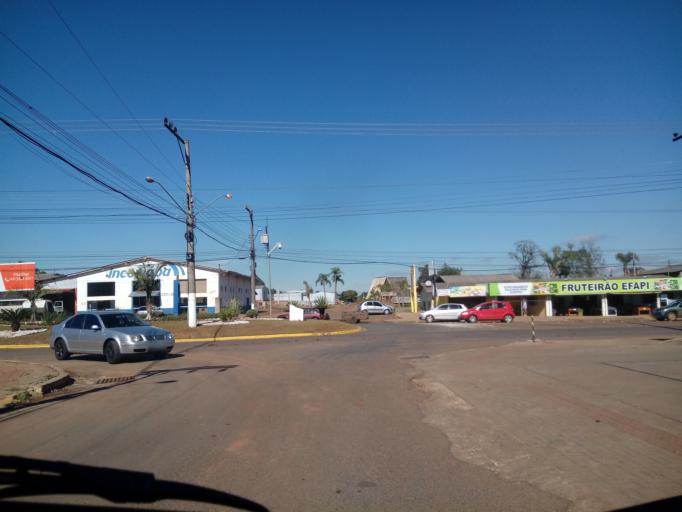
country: BR
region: Santa Catarina
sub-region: Chapeco
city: Chapeco
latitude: -27.0944
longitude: -52.6818
